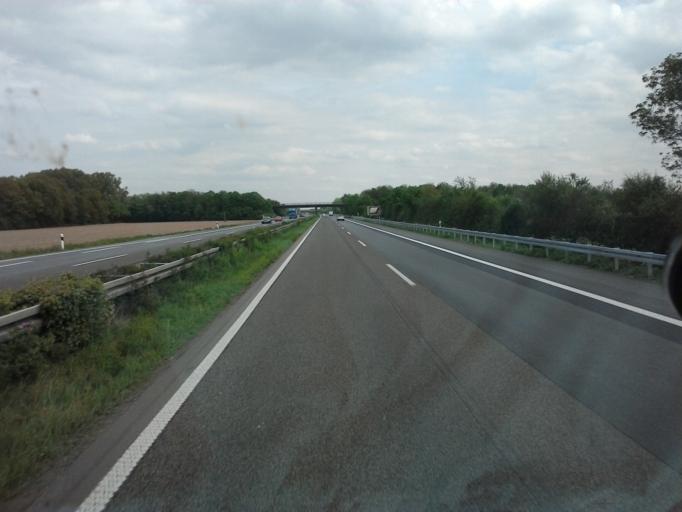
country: DE
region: North Rhine-Westphalia
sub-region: Regierungsbezirk Dusseldorf
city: Goch
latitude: 51.6694
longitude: 6.1246
